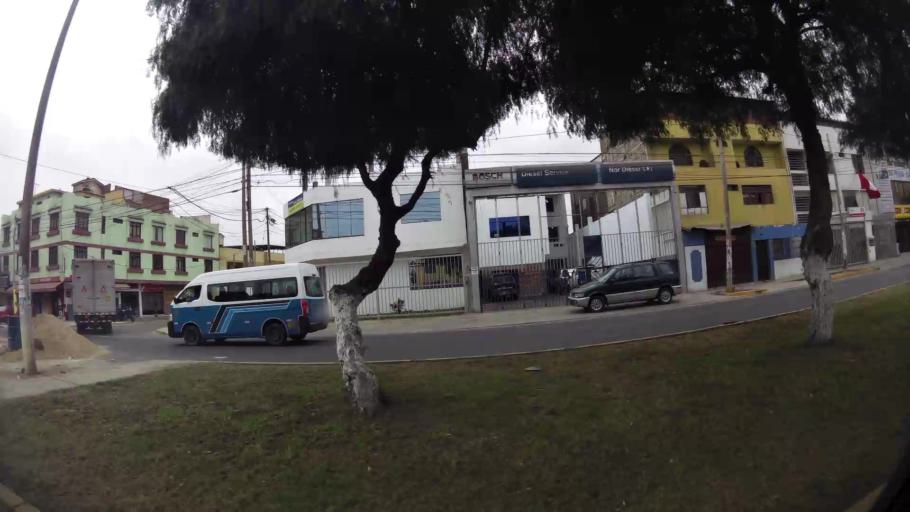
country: PE
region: La Libertad
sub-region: Provincia de Trujillo
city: Trujillo
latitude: -8.1204
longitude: -79.0197
